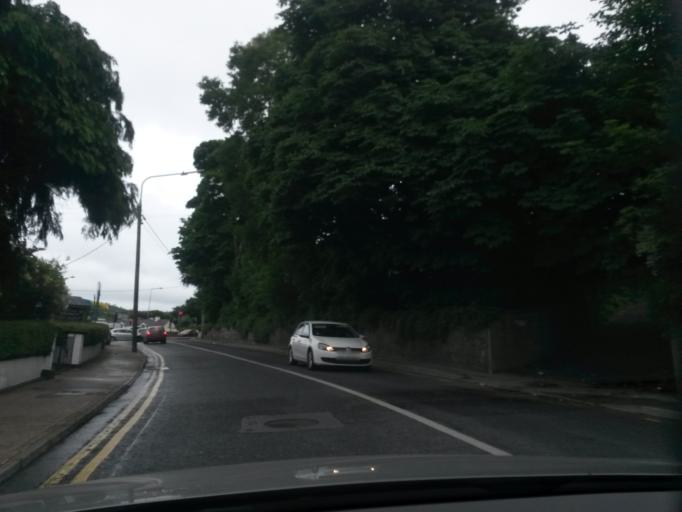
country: IE
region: Connaught
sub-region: Sligo
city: Sligo
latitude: 54.2634
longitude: -8.4692
